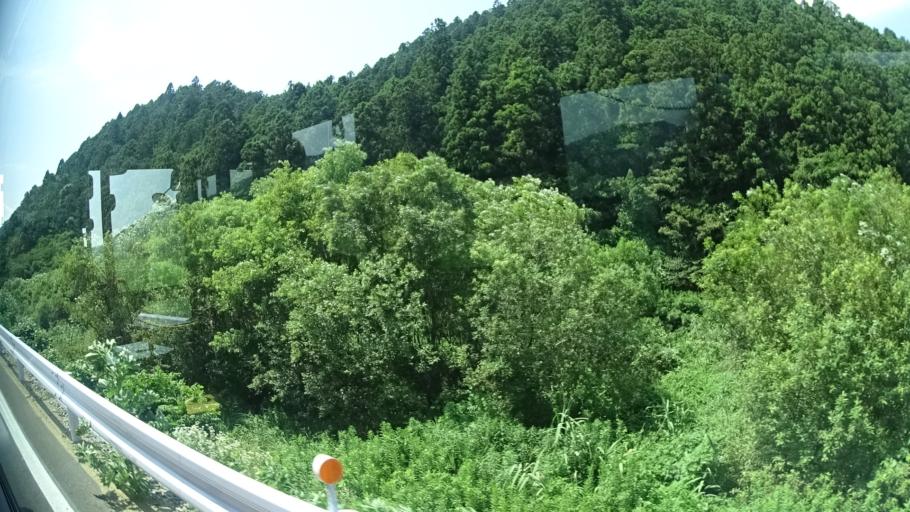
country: JP
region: Miyagi
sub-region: Oshika Gun
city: Onagawa Cho
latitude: 38.6248
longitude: 141.3319
